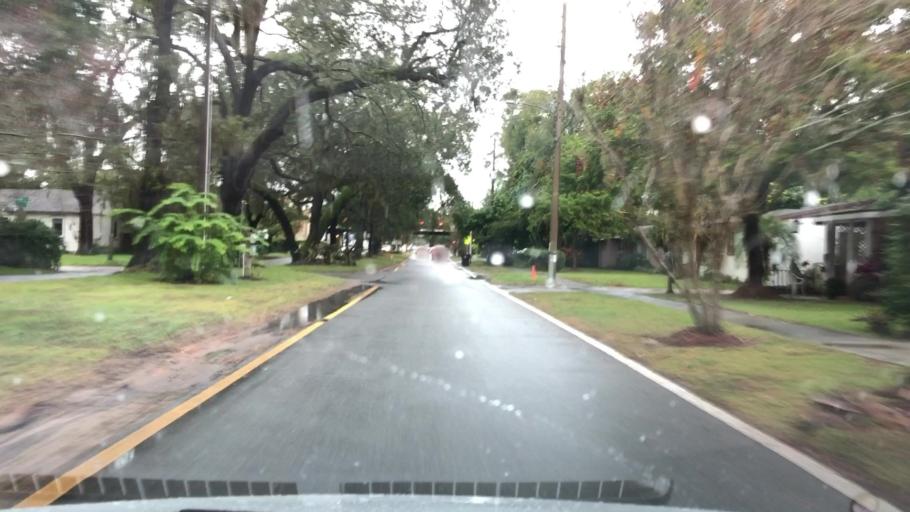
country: US
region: Florida
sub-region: Orange County
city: Orlando
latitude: 28.5364
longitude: -81.3476
